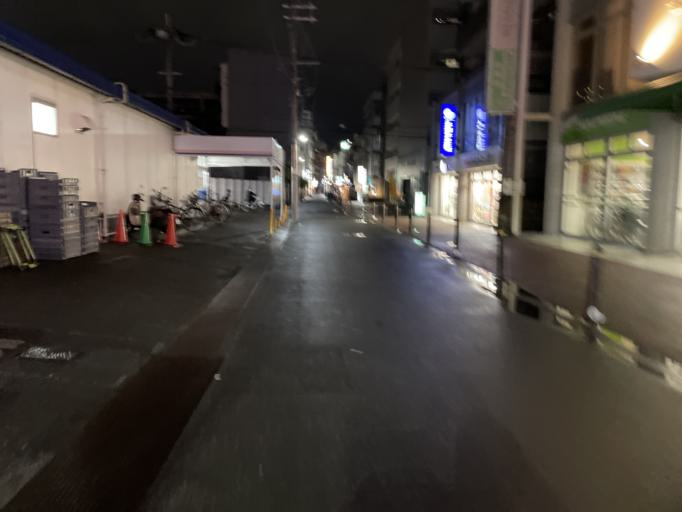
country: JP
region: Osaka
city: Ibaraki
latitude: 34.8158
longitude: 135.5792
